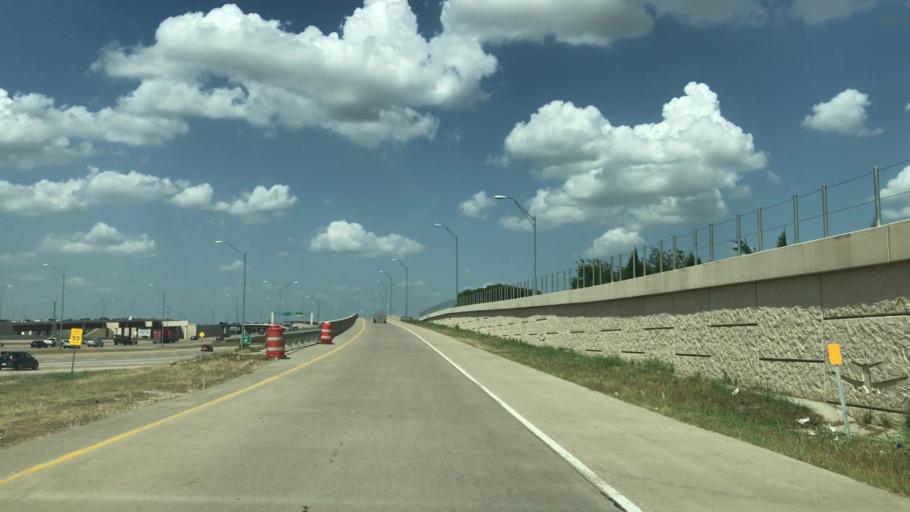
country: US
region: Texas
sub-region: Tarrant County
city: Grapevine
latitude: 32.9287
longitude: -97.0488
